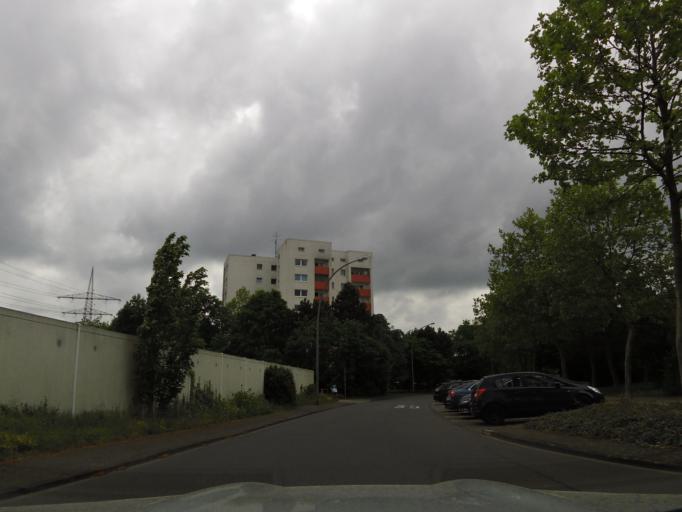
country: DE
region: Hesse
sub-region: Regierungsbezirk Darmstadt
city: Florsheim
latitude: 50.0067
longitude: 8.4399
